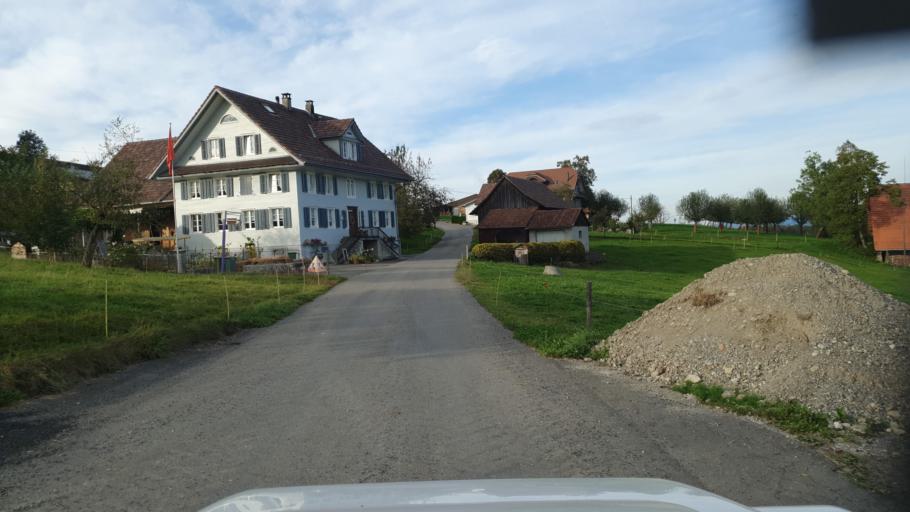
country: CH
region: Lucerne
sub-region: Hochdorf District
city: Hohenrain
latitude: 47.1872
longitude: 8.3471
